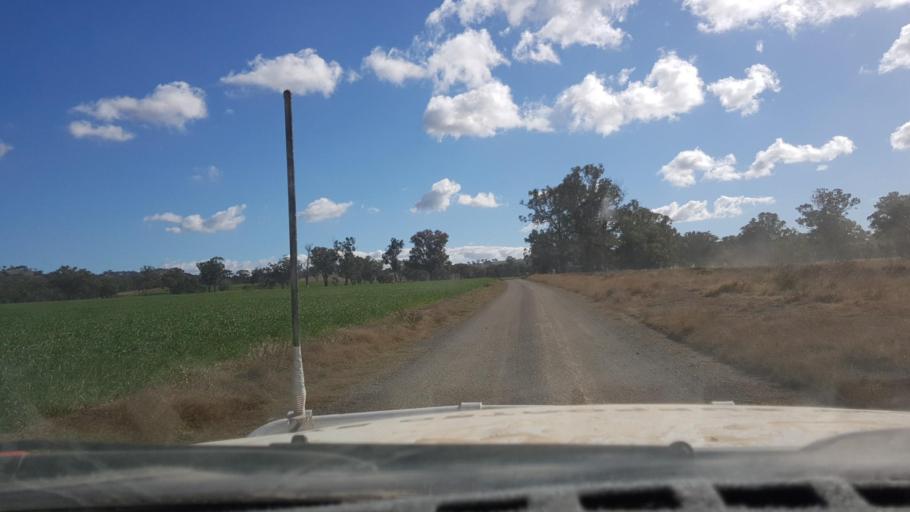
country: AU
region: New South Wales
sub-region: Narrabri
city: Blair Athol
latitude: -30.5778
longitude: 150.4721
